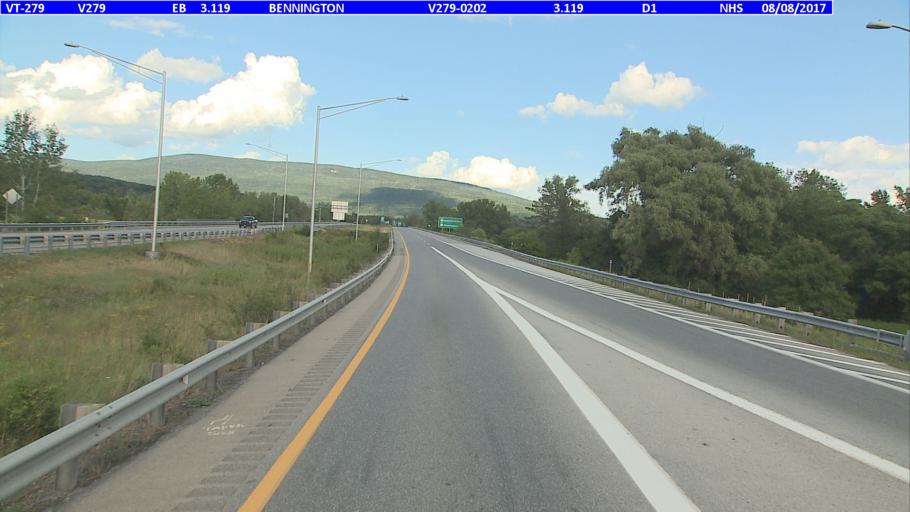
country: US
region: Vermont
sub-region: Bennington County
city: North Bennington
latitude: 42.9048
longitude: -73.2195
